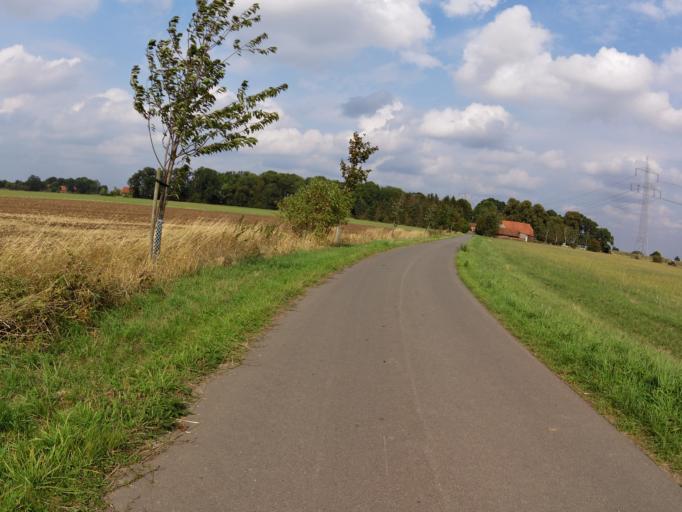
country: DE
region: Lower Saxony
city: Hilgermissen
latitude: 52.8815
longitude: 9.1767
